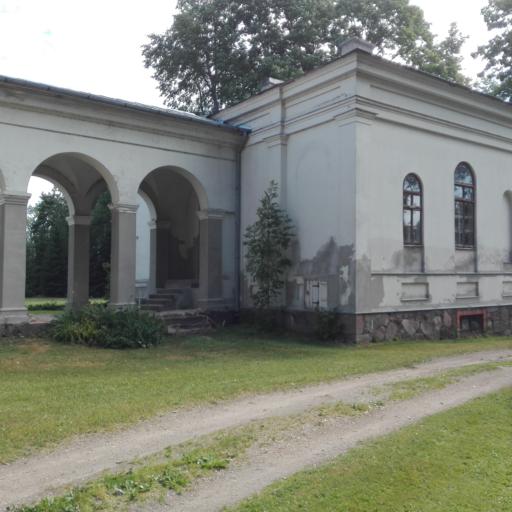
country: LT
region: Panevezys
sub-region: Birzai
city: Birzai
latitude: 56.2191
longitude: 24.7689
